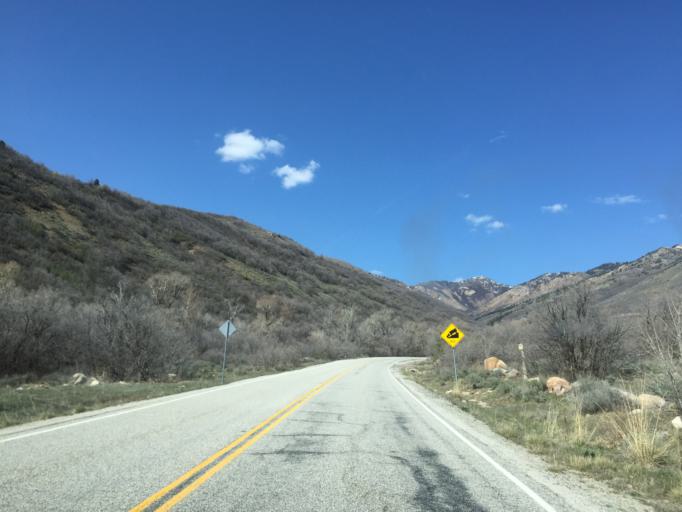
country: US
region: Utah
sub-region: Weber County
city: Wolf Creek
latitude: 41.3409
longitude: -111.8254
